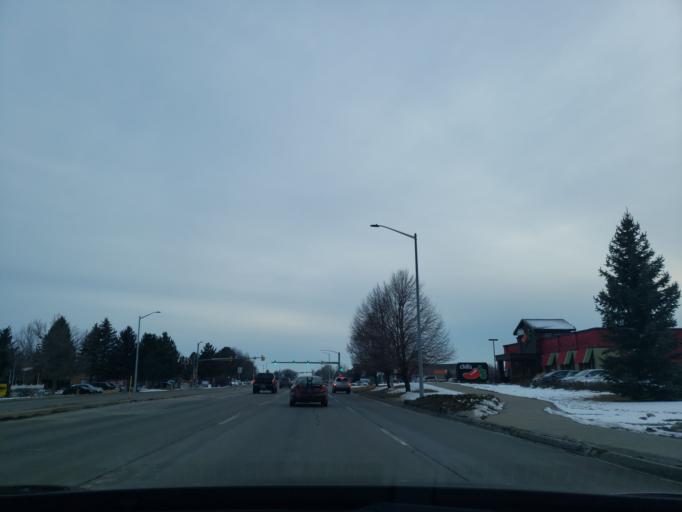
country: US
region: Colorado
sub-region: Boulder County
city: Longmont
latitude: 40.1453
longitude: -105.1309
